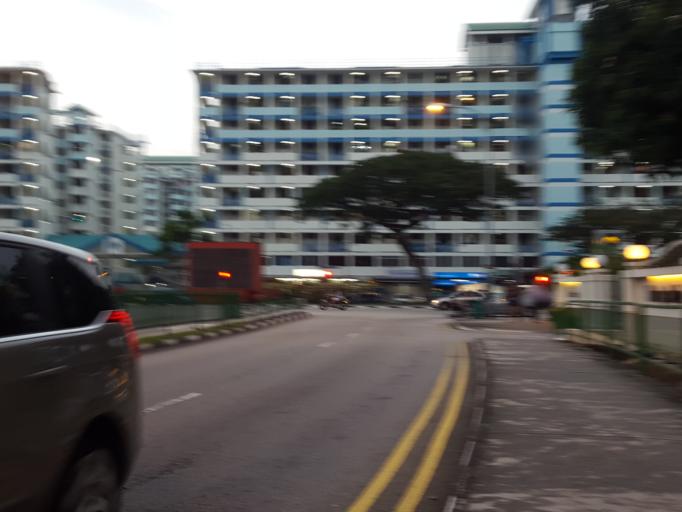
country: SG
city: Singapore
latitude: 1.3404
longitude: 103.8471
